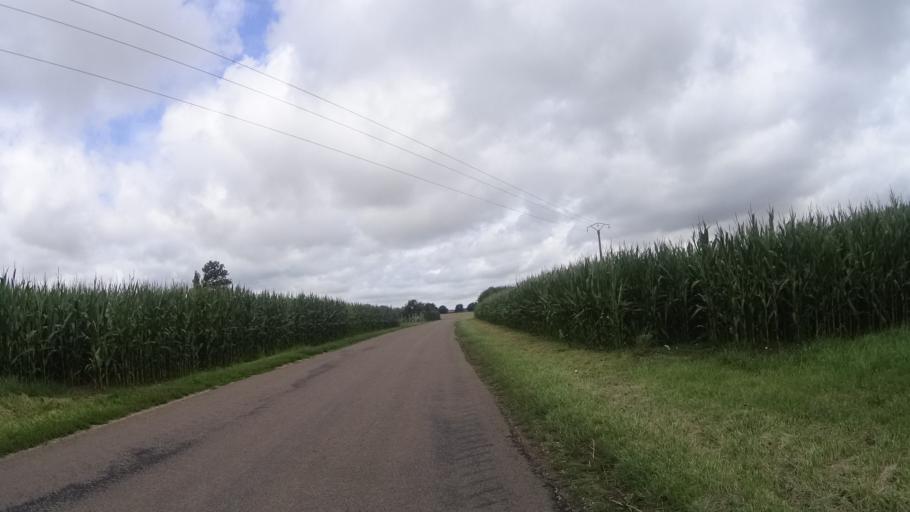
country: FR
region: Champagne-Ardenne
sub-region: Departement de l'Aube
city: Ervy-le-Chatel
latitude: 48.0865
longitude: 3.9578
